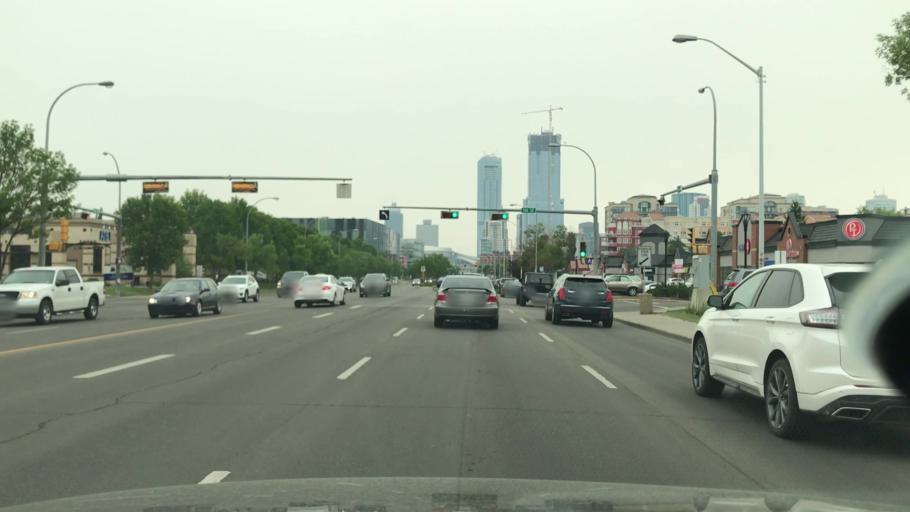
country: CA
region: Alberta
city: Edmonton
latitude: 53.5461
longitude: -113.5184
